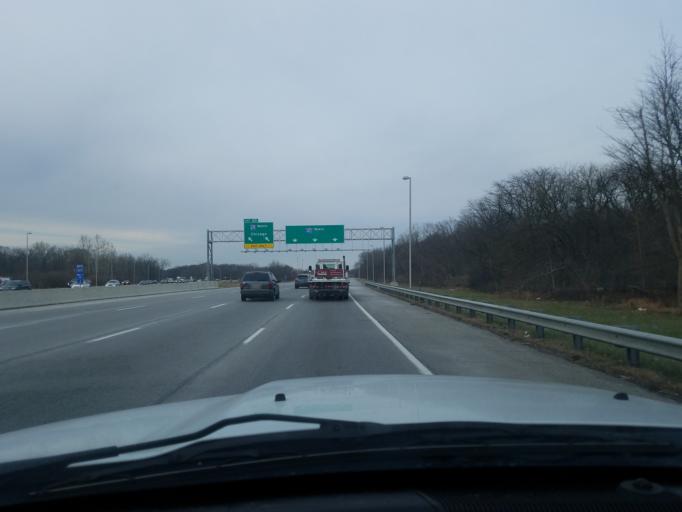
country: US
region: Indiana
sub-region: Marion County
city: Speedway
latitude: 39.8559
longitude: -86.2761
